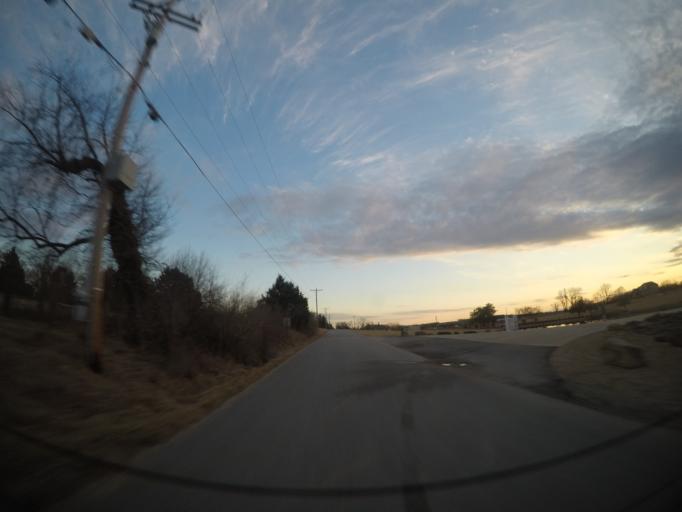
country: US
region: Kansas
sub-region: Wyandotte County
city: Bonner Springs
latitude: 39.0460
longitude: -94.9088
